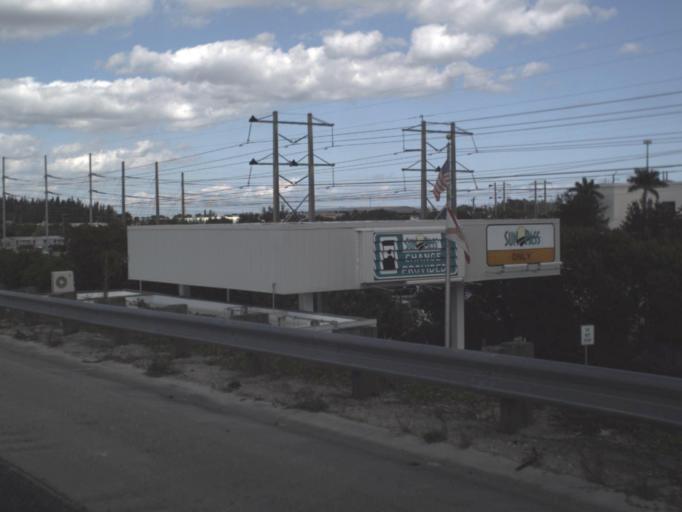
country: US
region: Florida
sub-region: Broward County
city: Davie
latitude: 26.0669
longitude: -80.2153
